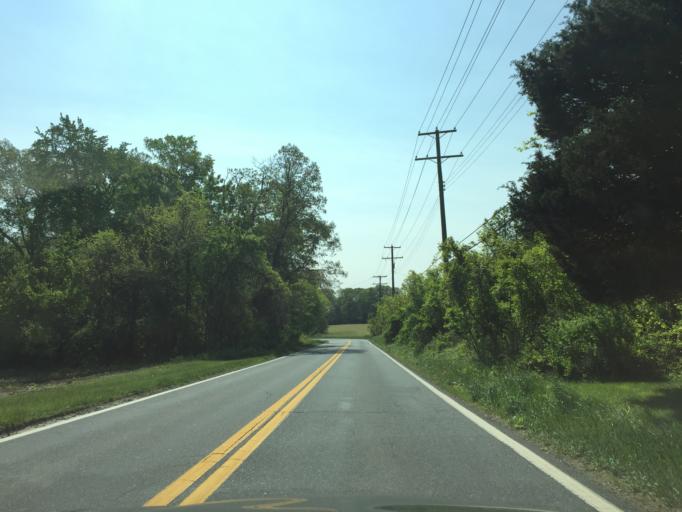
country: US
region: Maryland
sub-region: Baltimore County
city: Bowleys Quarters
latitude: 39.3644
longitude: -76.4005
